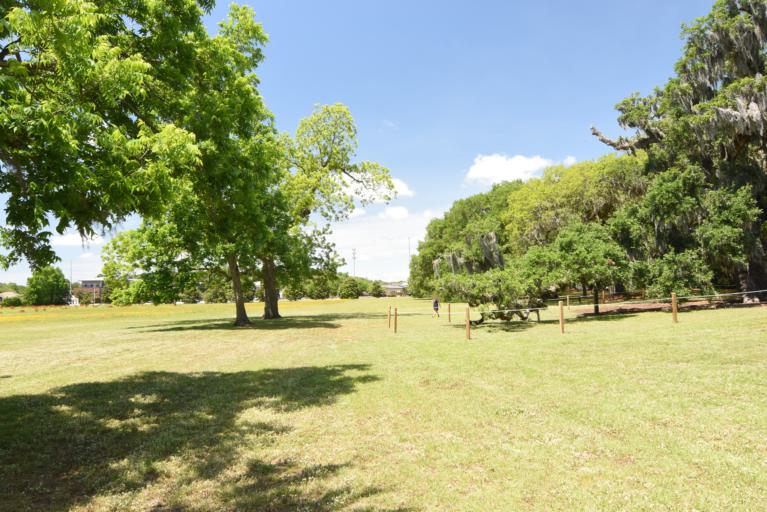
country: US
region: South Carolina
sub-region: Charleston County
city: Charleston
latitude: 32.7624
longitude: -79.9723
